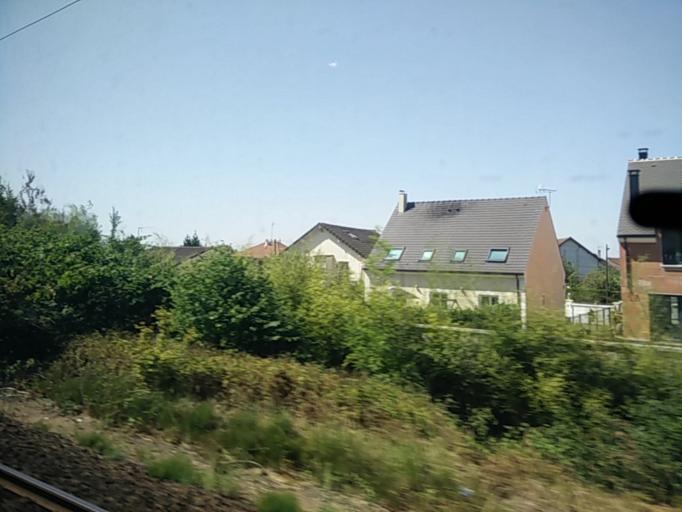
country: FR
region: Ile-de-France
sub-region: Departement de Seine-et-Marne
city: Ozoir-la-Ferriere
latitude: 48.7764
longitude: 2.6878
